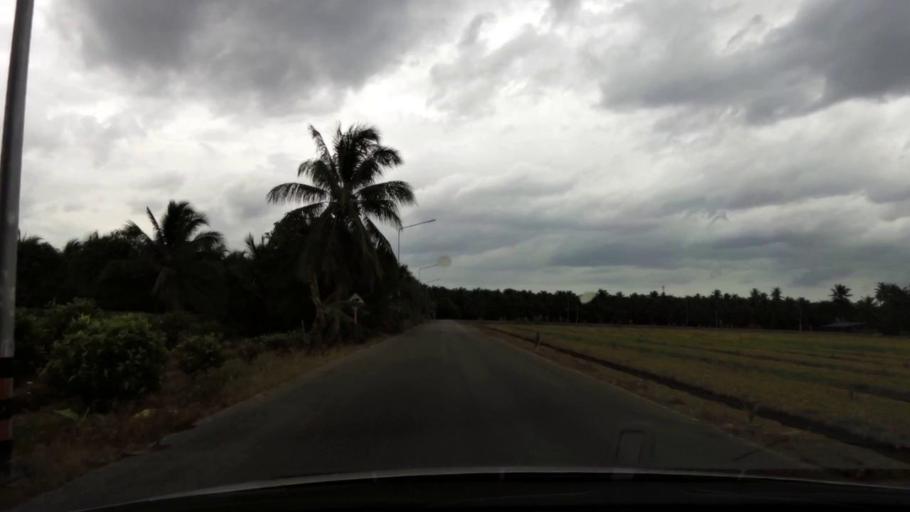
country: TH
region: Ratchaburi
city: Damnoen Saduak
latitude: 13.5754
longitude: 99.9811
